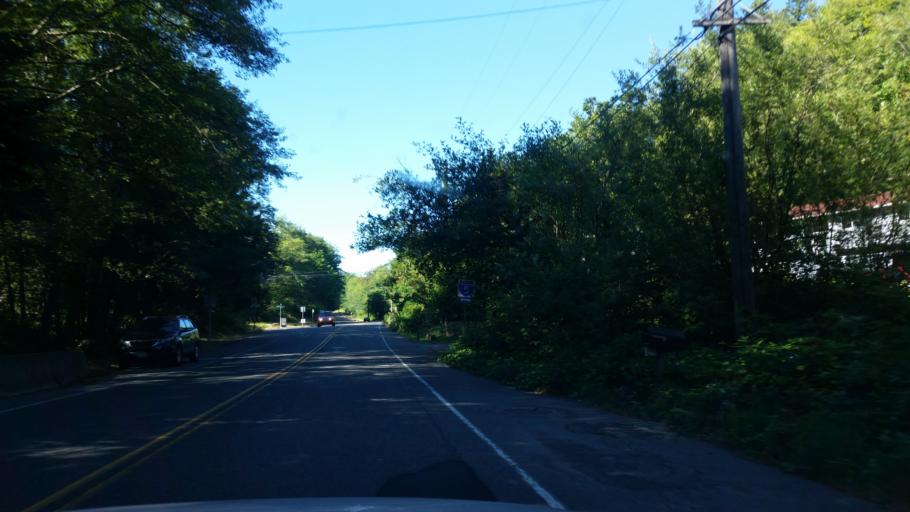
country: US
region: Washington
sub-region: Snohomish County
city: Brier
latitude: 47.7766
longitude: -122.2902
